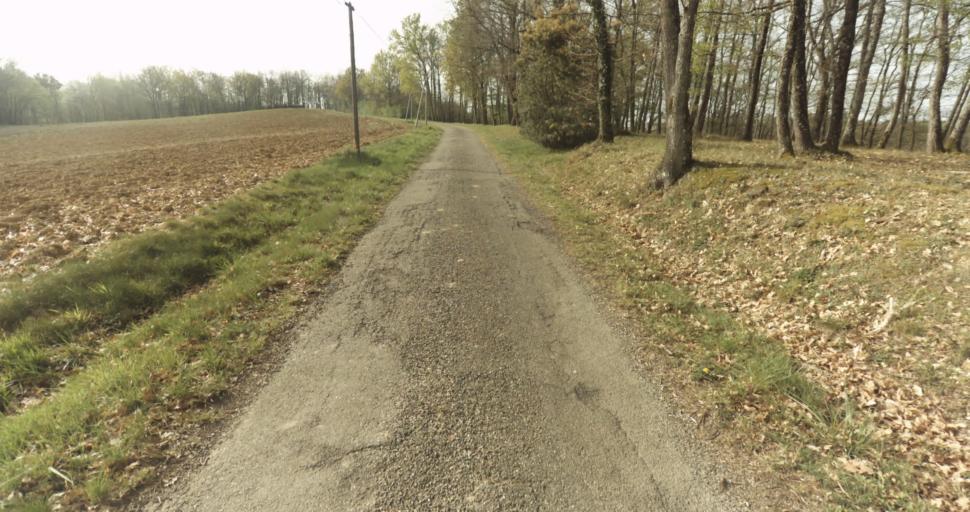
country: FR
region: Midi-Pyrenees
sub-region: Departement du Tarn-et-Garonne
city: Moissac
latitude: 44.1610
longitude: 1.0378
